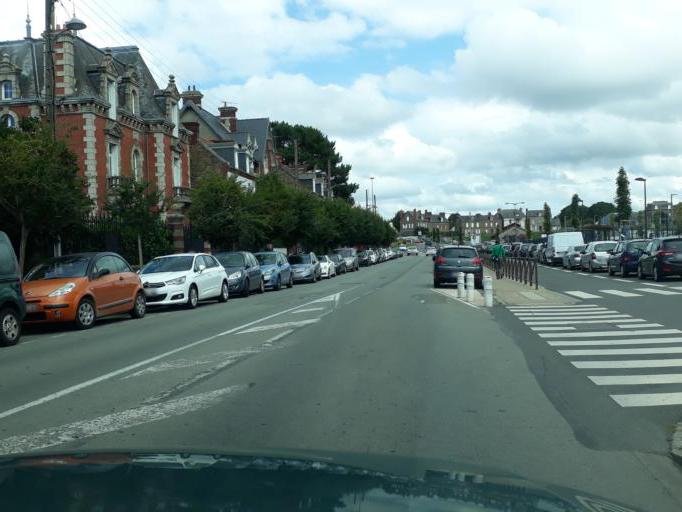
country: FR
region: Brittany
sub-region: Departement des Cotes-d'Armor
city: Lamballe
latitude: 48.4664
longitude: -2.5112
